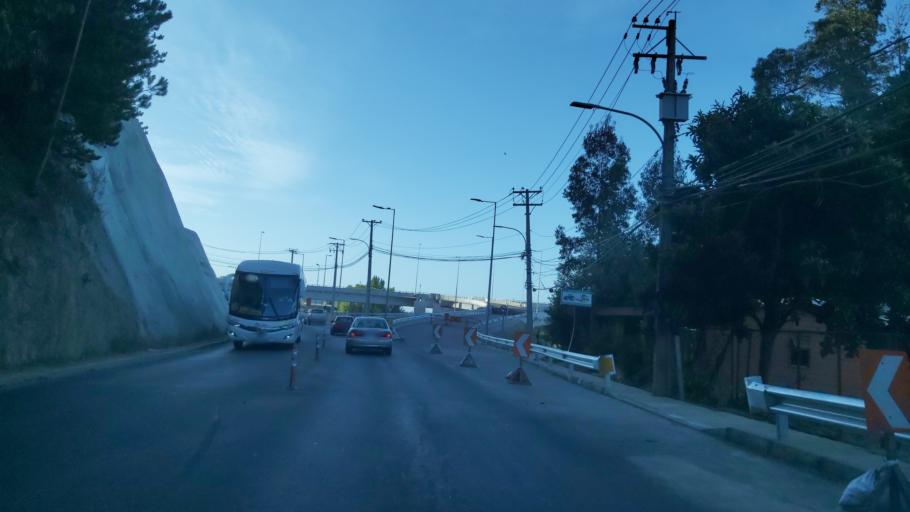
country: CL
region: Biobio
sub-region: Provincia de Concepcion
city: Concepcion
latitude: -36.8443
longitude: -73.0753
